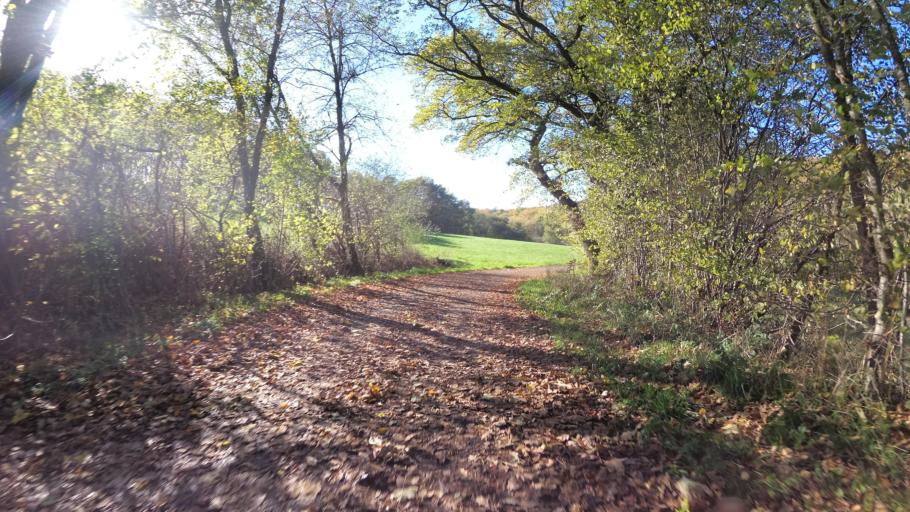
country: DE
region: Saarland
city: Mainzweiler
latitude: 49.4117
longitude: 7.0782
